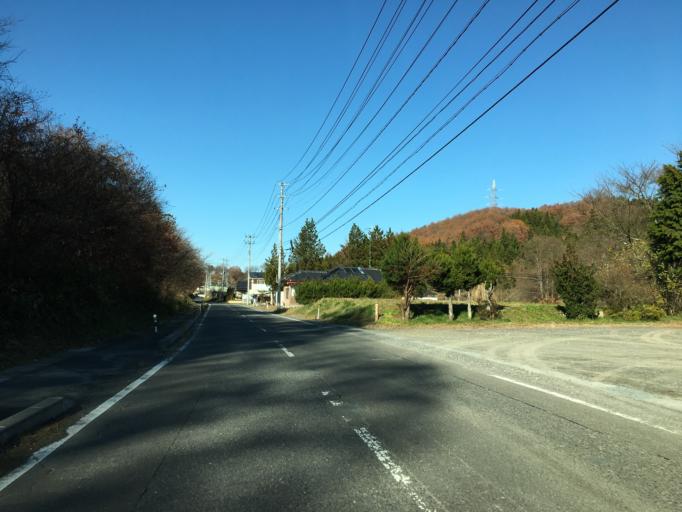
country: JP
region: Fukushima
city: Ishikawa
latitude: 37.2267
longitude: 140.5678
